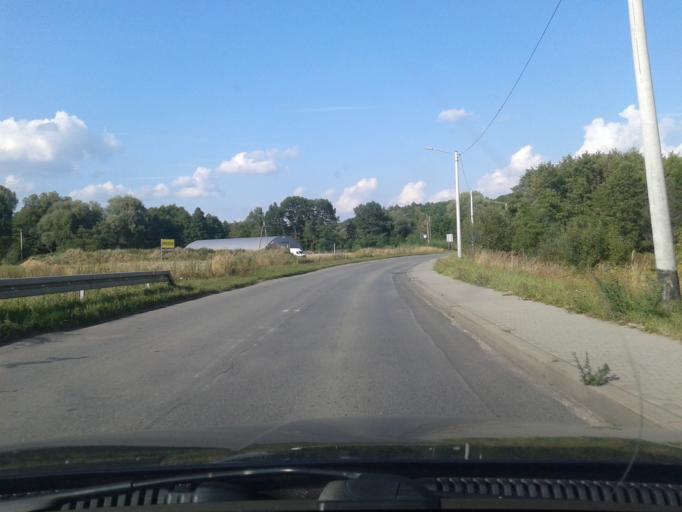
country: PL
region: Silesian Voivodeship
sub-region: Powiat wodzislawski
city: Wodzislaw Slaski
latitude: 50.0030
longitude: 18.4790
